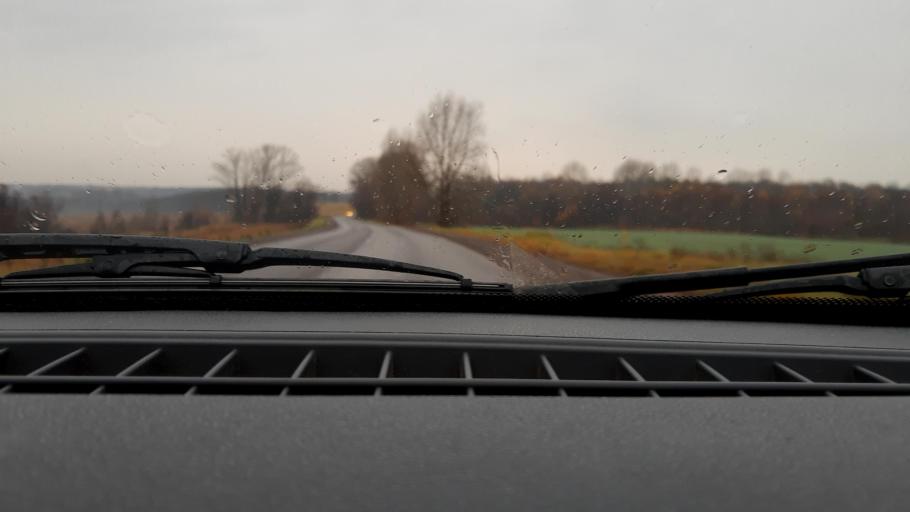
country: RU
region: Bashkortostan
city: Mikhaylovka
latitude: 54.8337
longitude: 55.9373
